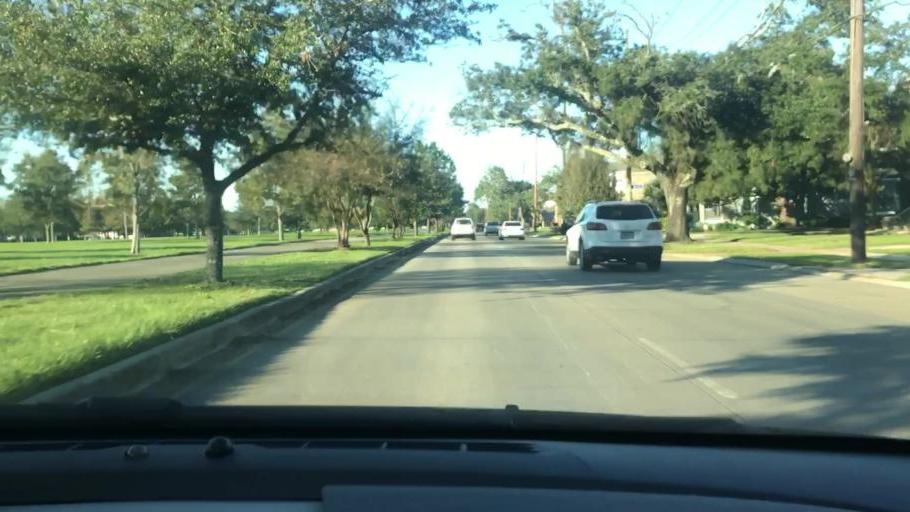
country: US
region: Louisiana
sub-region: Jefferson Parish
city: Metairie
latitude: 30.0010
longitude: -90.1150
